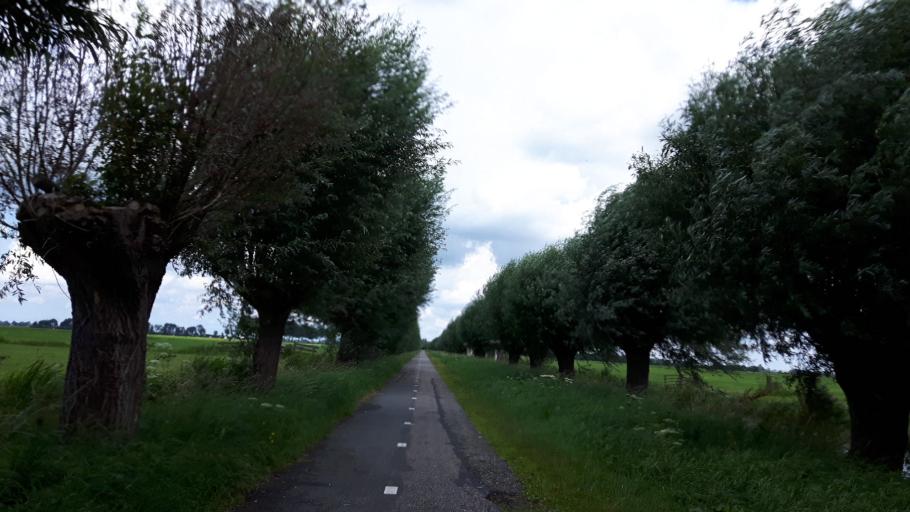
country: NL
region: Utrecht
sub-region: Gemeente Woerden
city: Woerden
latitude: 52.1092
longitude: 4.9199
